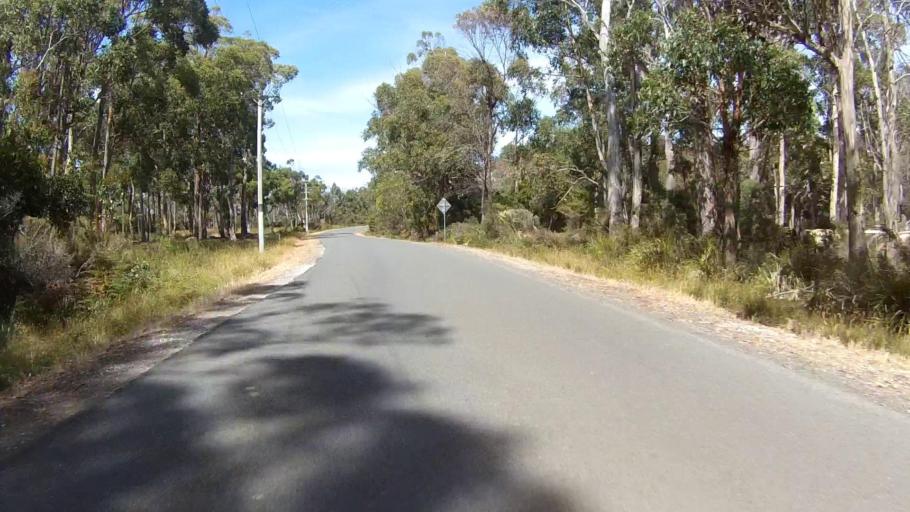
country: AU
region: Tasmania
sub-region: Huon Valley
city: Cygnet
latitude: -43.2399
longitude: 147.1240
